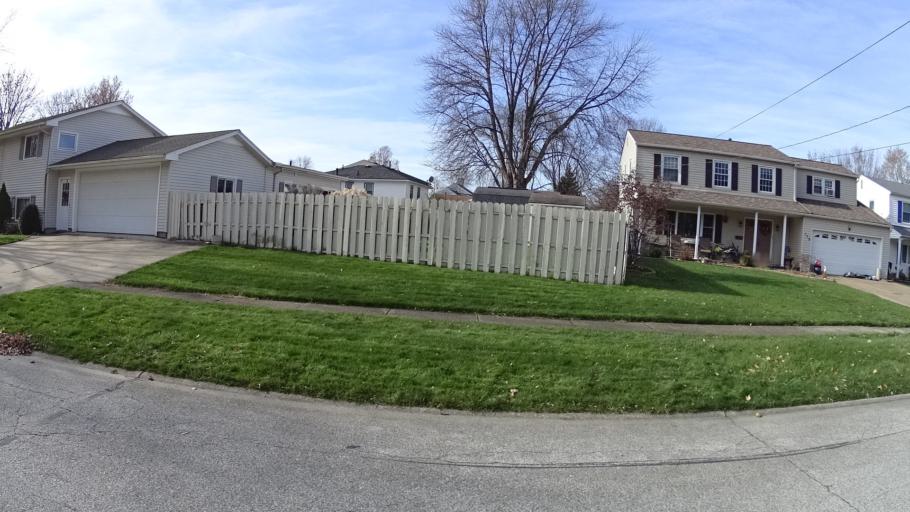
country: US
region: Ohio
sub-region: Lorain County
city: Sheffield
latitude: 41.4017
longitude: -82.0849
